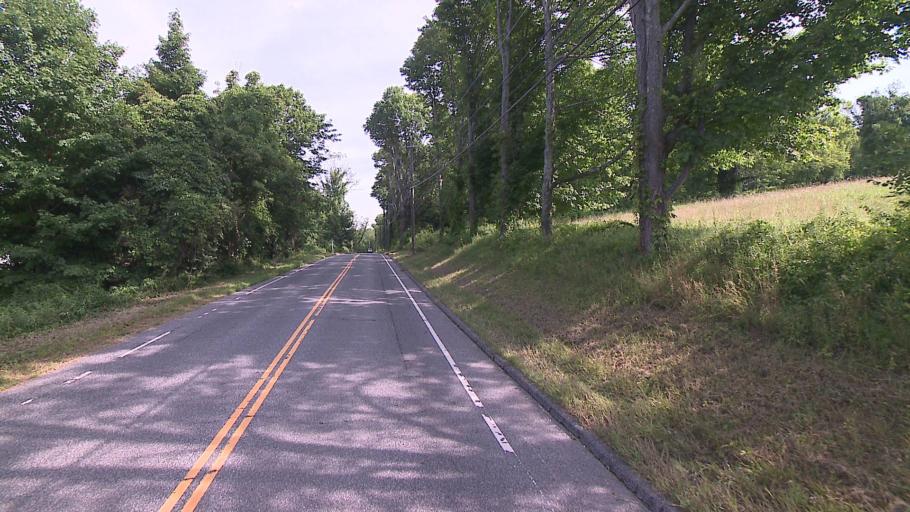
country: US
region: Connecticut
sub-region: Fairfield County
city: Sherman
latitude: 41.5566
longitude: -73.5040
